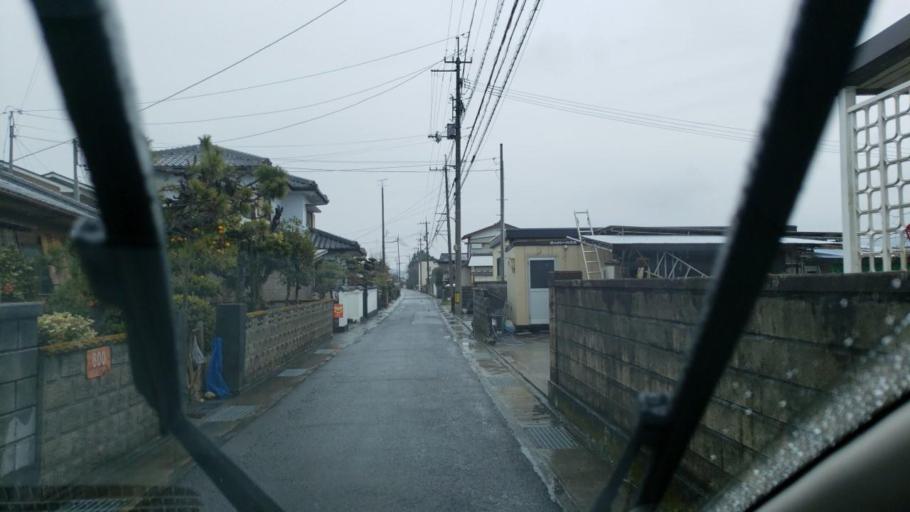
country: JP
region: Tokushima
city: Kamojimacho-jogejima
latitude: 34.0769
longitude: 134.3438
